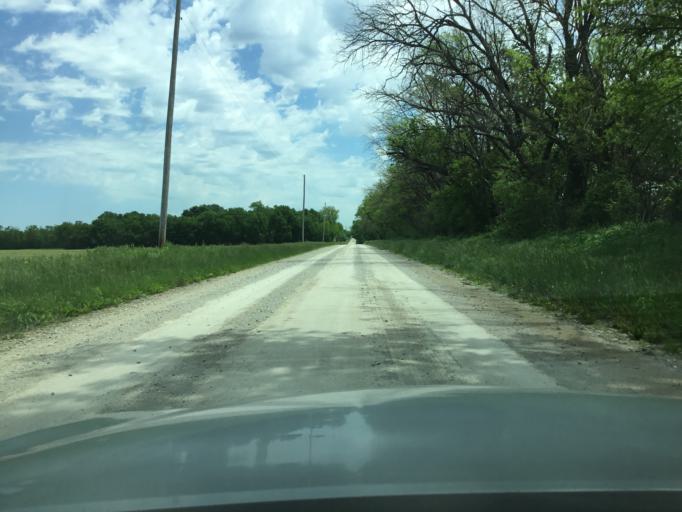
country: US
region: Kansas
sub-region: Montgomery County
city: Independence
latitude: 37.1095
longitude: -95.7689
